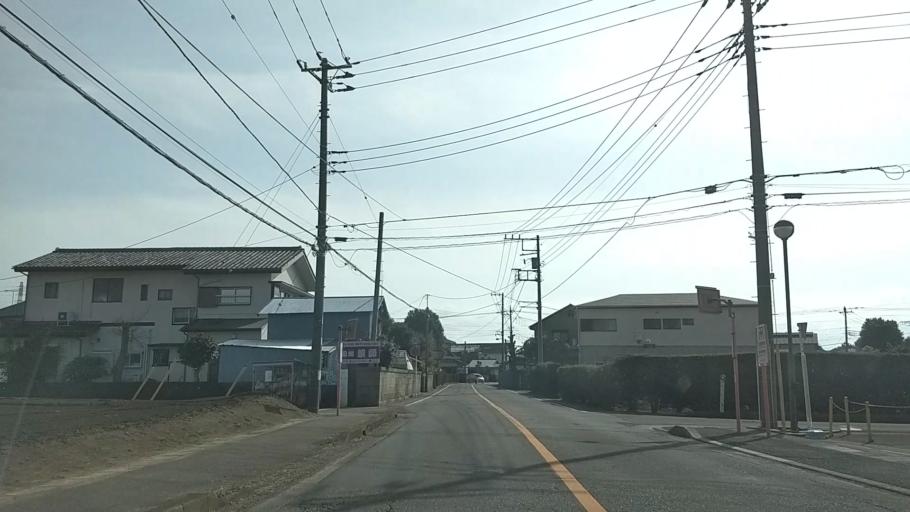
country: JP
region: Kanagawa
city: Chigasaki
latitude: 35.3560
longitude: 139.3845
